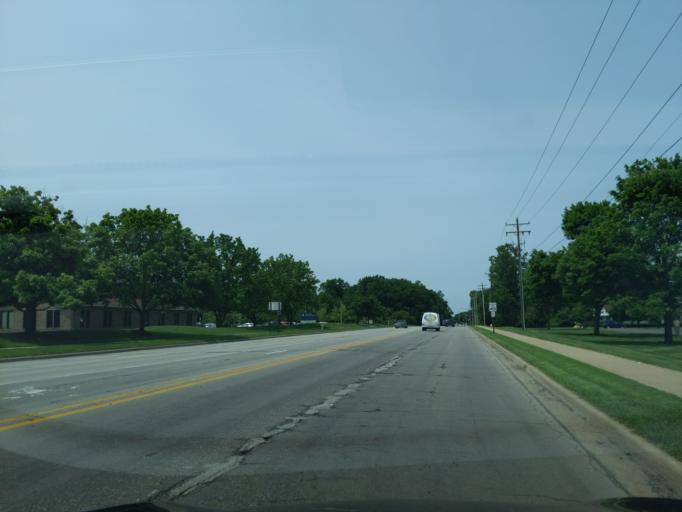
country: US
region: Michigan
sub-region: Eaton County
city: Waverly
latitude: 42.7339
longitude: -84.6328
